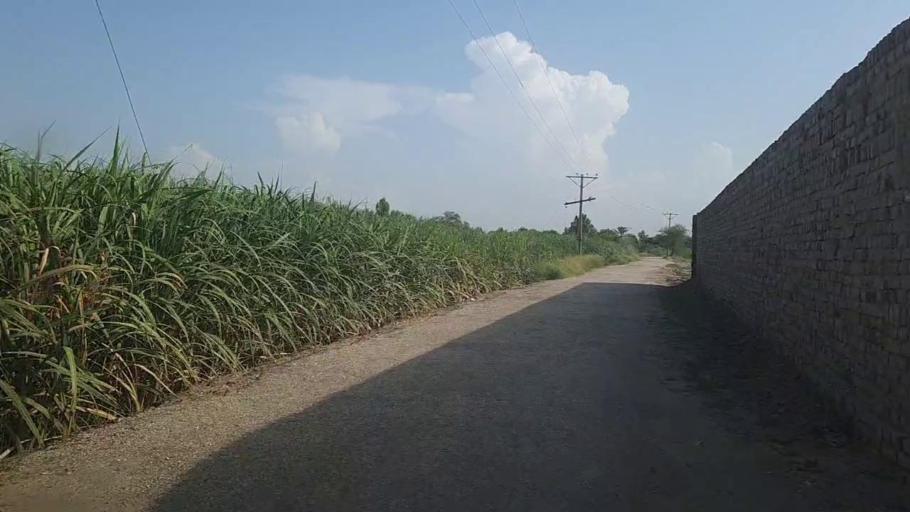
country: PK
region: Sindh
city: Ubauro
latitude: 28.1681
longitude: 69.7739
